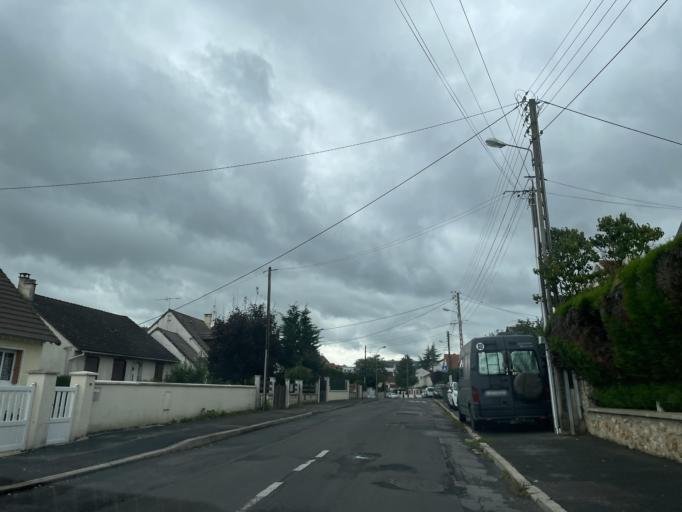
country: FR
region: Ile-de-France
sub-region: Departement de Seine-et-Marne
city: Coulommiers
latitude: 48.8201
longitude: 3.0996
